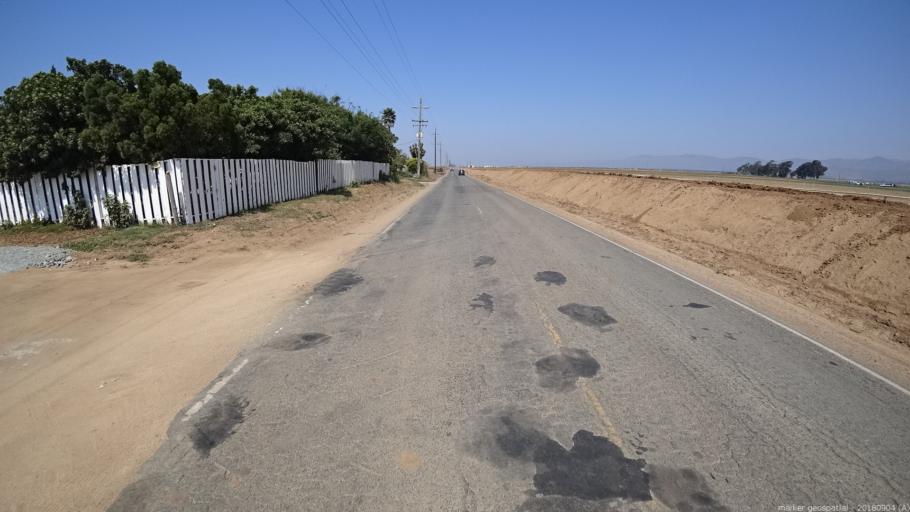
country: US
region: California
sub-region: Monterey County
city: Chualar
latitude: 36.5522
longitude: -121.4746
